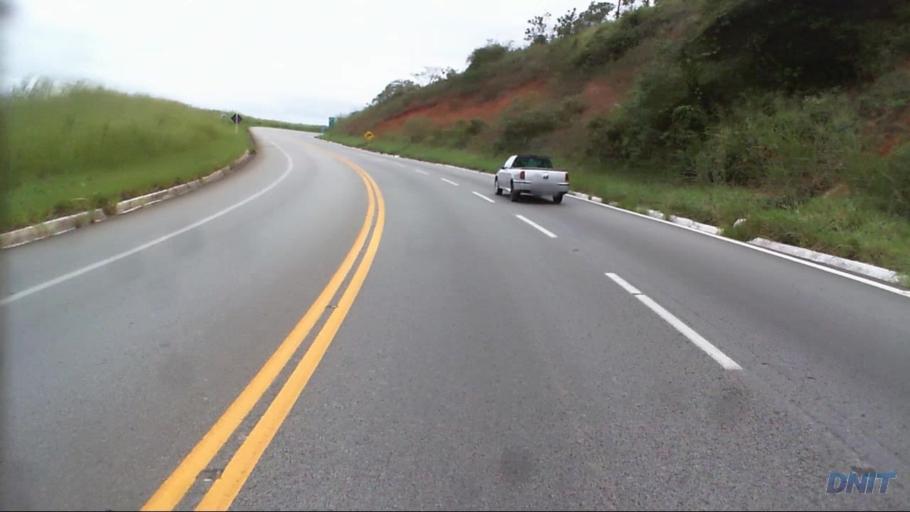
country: BR
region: Minas Gerais
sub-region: Nova Era
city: Nova Era
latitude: -19.8029
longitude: -43.0608
